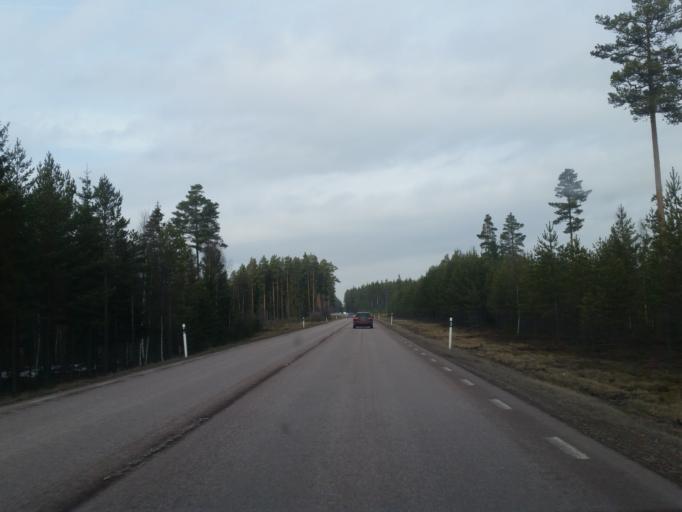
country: SE
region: Dalarna
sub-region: Mora Kommun
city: Mora
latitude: 60.9760
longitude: 14.6951
